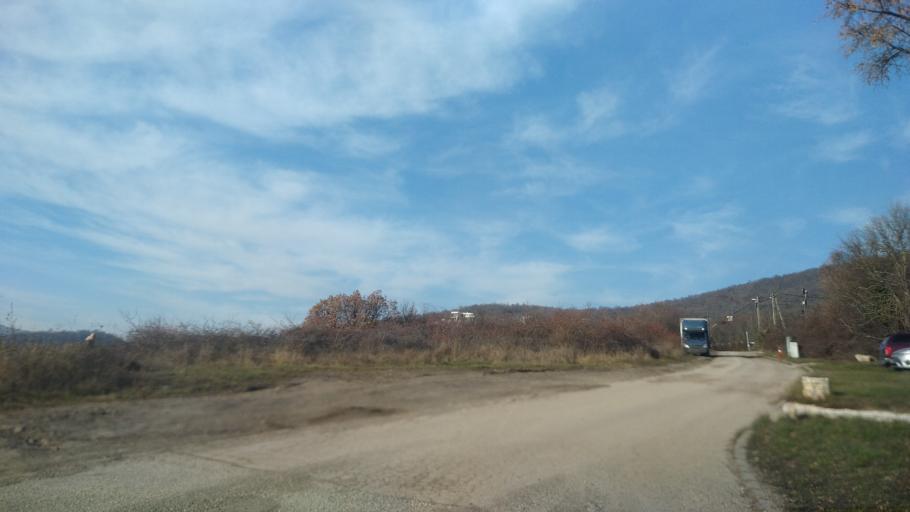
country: HU
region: Pest
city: Leanyfalu
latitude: 47.7004
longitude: 19.0510
